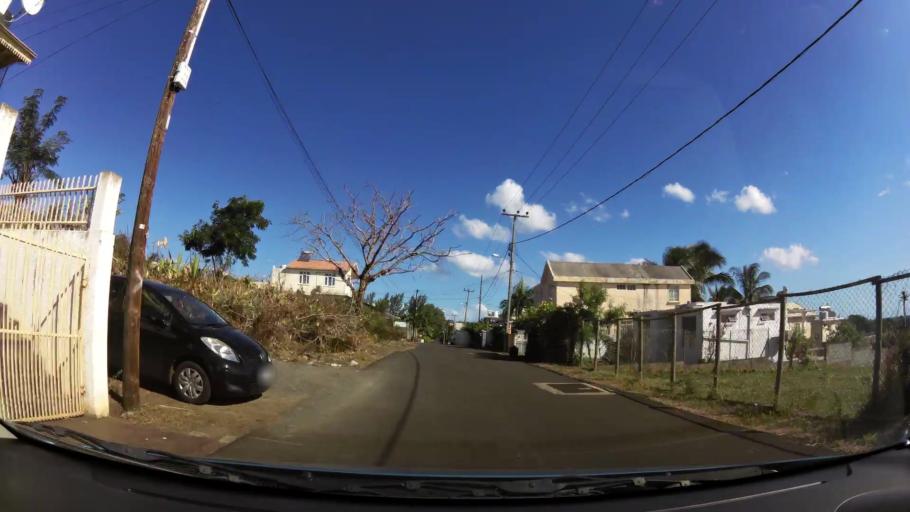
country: MU
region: Black River
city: Albion
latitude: -20.2159
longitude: 57.4073
